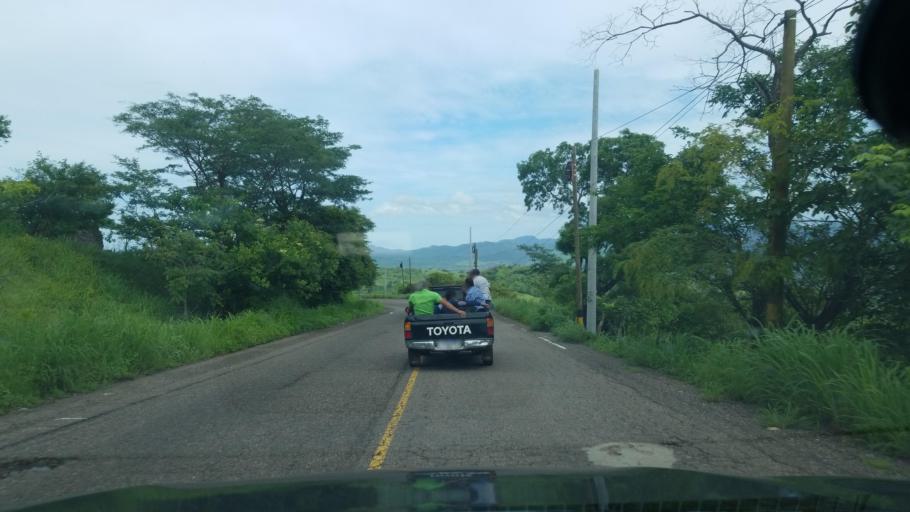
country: HN
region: Choluteca
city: Corpus
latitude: 13.3768
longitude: -87.0565
